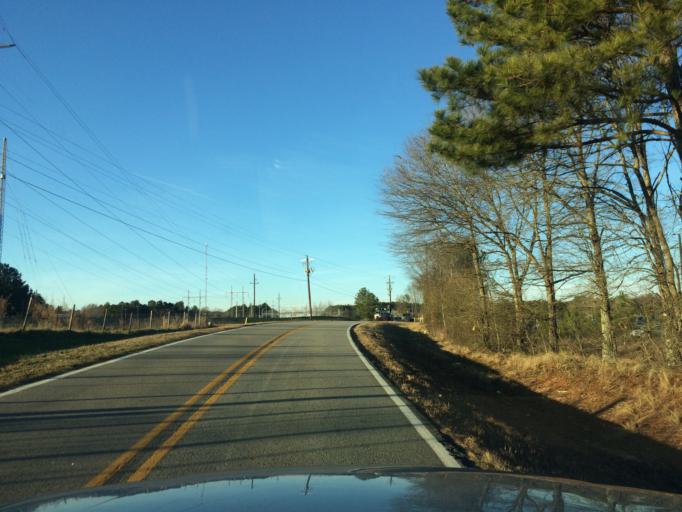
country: US
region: Georgia
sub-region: Barrow County
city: Winder
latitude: 33.9891
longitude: -83.7524
